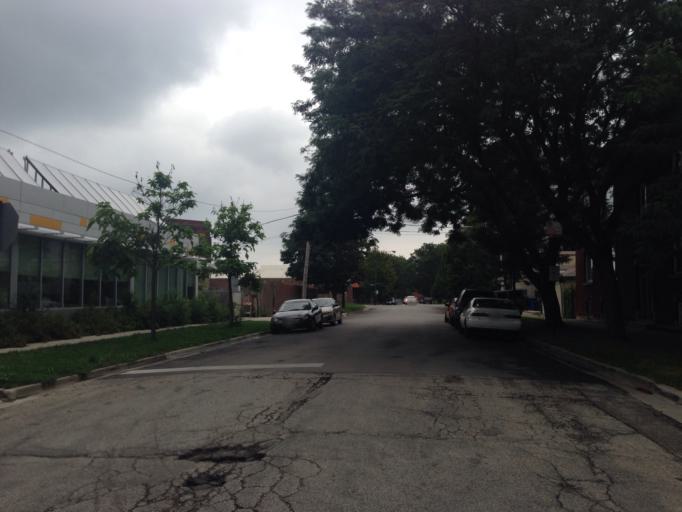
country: US
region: Illinois
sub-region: Cook County
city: Lincolnwood
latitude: 41.9340
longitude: -87.6919
